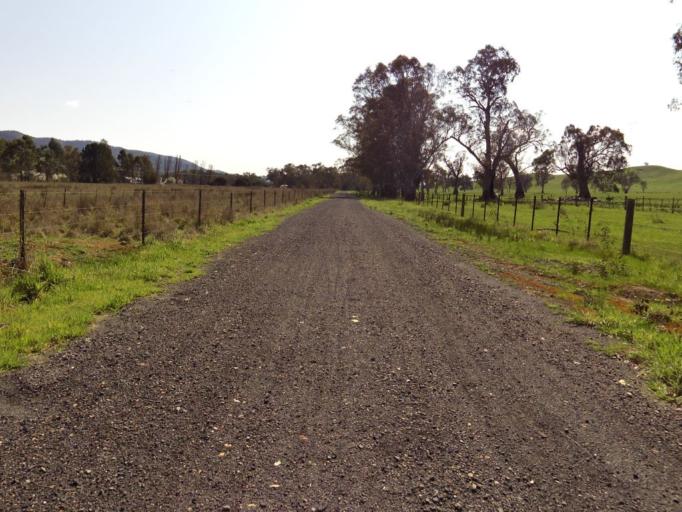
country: AU
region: Victoria
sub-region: Murrindindi
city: Alexandra
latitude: -37.1463
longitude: 145.5880
